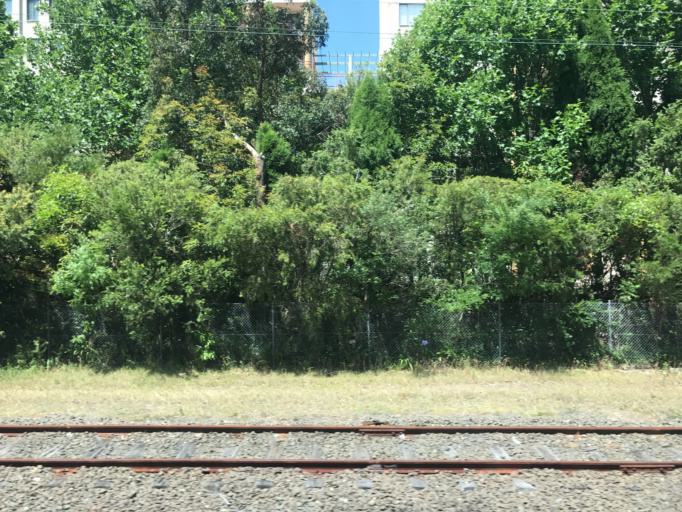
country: AU
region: New South Wales
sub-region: North Sydney
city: St Leonards
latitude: -33.8194
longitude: 151.1936
